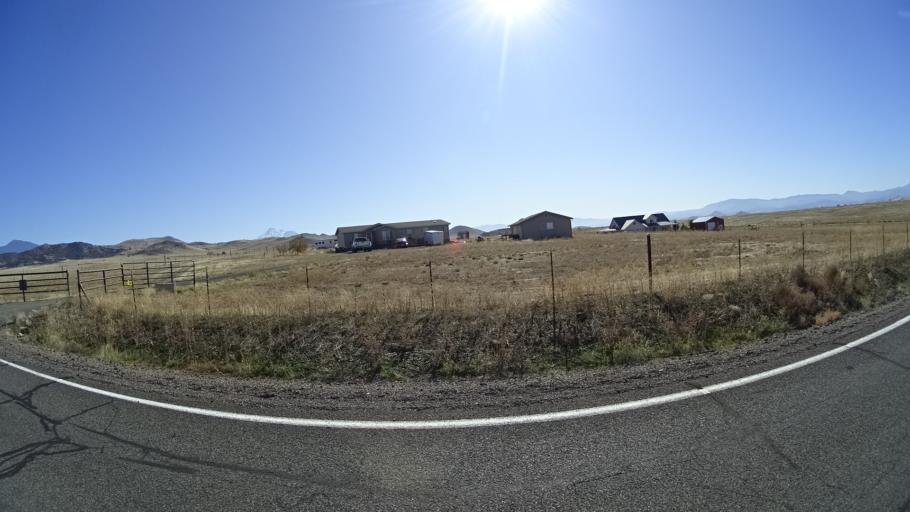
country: US
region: California
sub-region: Siskiyou County
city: Montague
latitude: 41.8079
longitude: -122.4290
